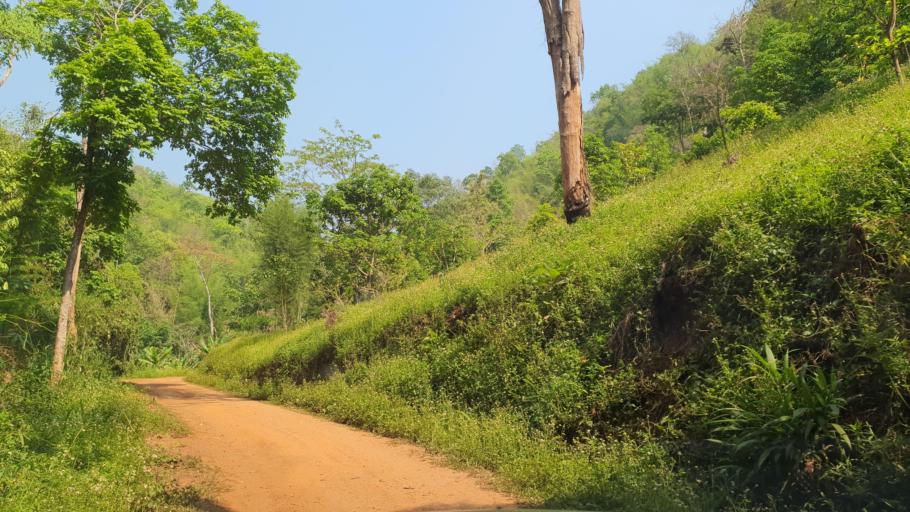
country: TH
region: Chiang Mai
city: Samoeng
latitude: 18.7938
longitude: 98.7968
